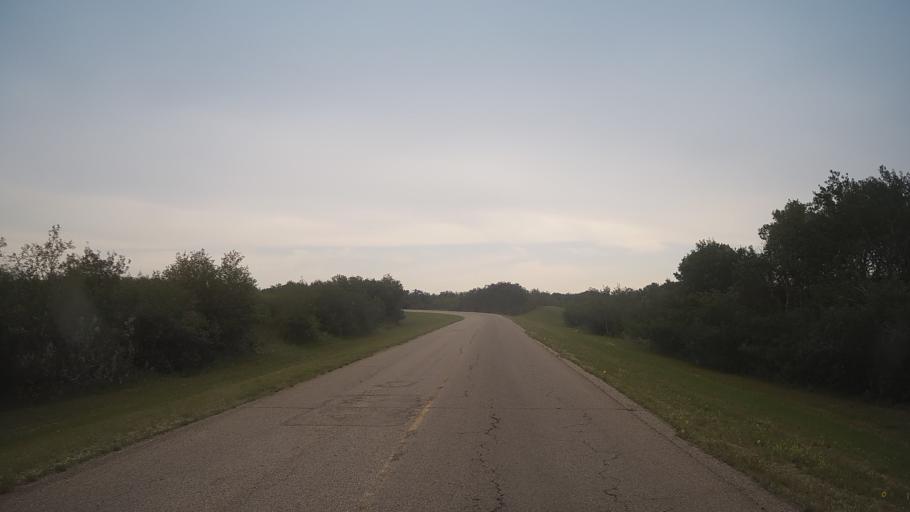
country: CA
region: Saskatchewan
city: Saskatoon
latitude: 51.8455
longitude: -106.5399
